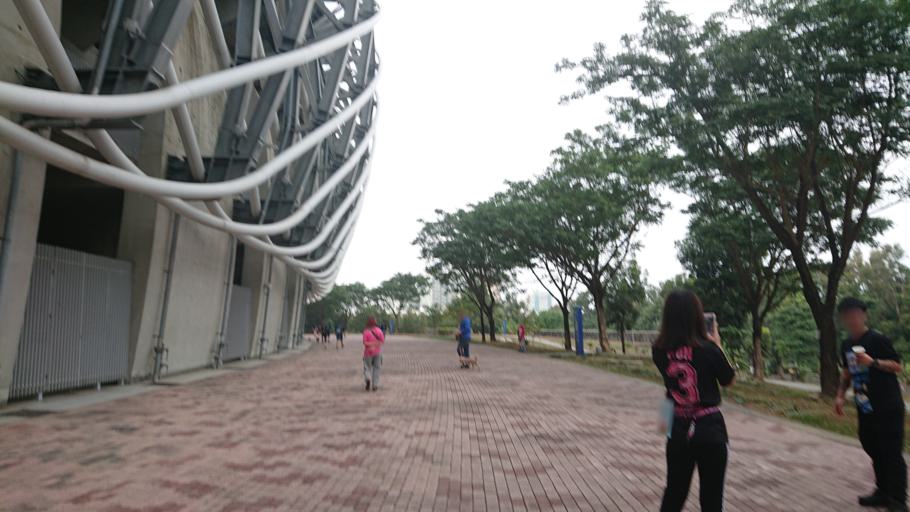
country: TW
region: Kaohsiung
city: Kaohsiung
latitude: 22.7036
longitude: 120.2955
